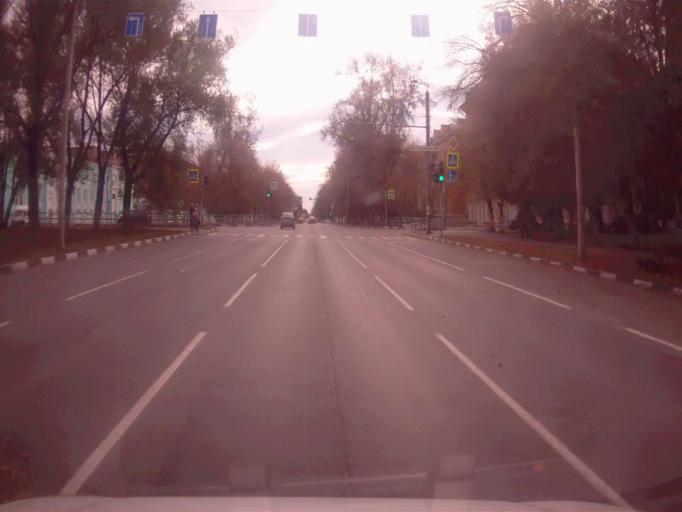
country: RU
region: Chelyabinsk
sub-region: Gorod Chelyabinsk
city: Chelyabinsk
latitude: 55.1232
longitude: 61.4739
